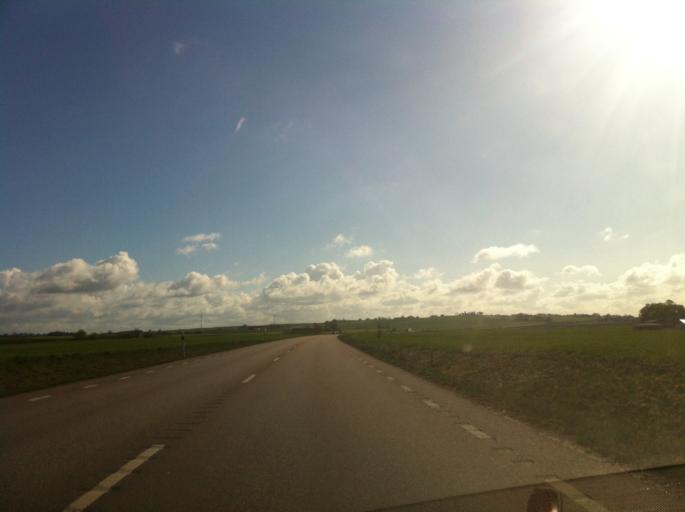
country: SE
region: Skane
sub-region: Svalovs Kommun
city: Teckomatorp
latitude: 55.8721
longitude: 13.1114
